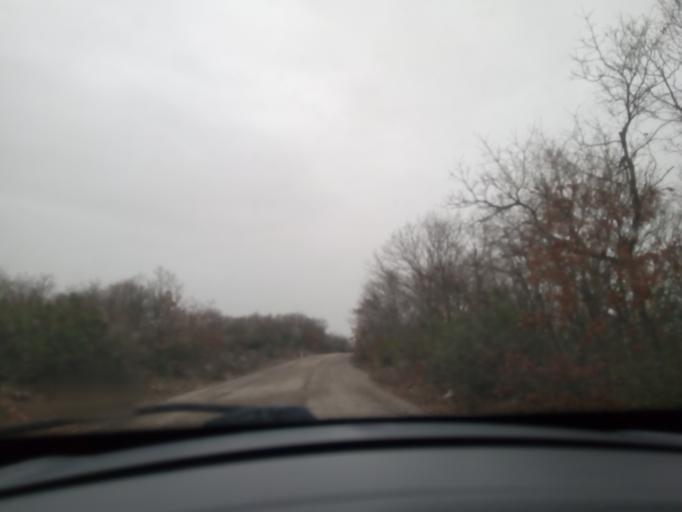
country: TR
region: Balikesir
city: Omerkoy
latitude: 39.9006
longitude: 28.0286
